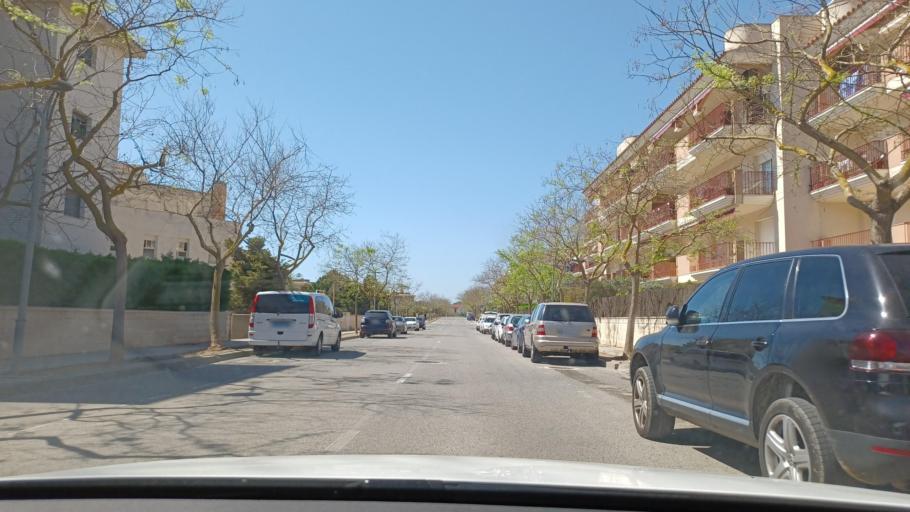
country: ES
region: Catalonia
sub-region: Provincia de Tarragona
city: Sant Carles de la Rapita
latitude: 40.6105
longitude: 0.5821
